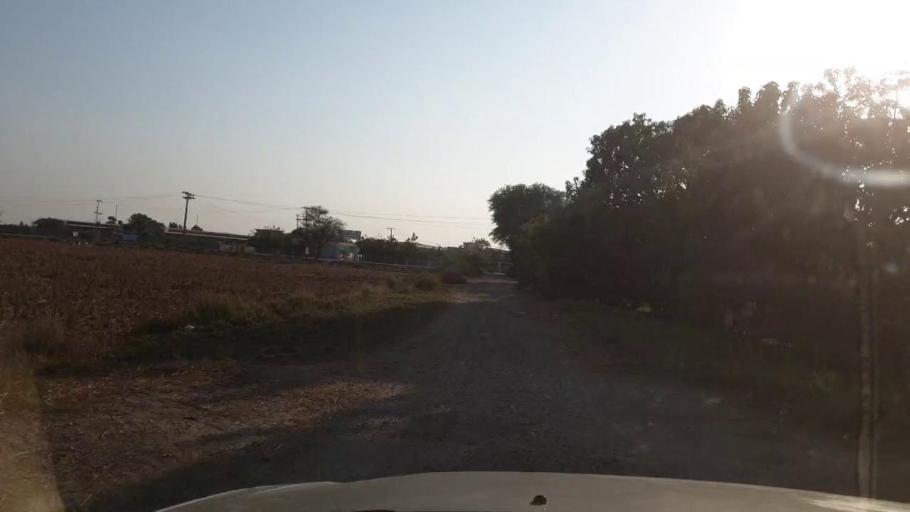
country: PK
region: Sindh
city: Tando Muhammad Khan
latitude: 25.1187
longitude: 68.5501
